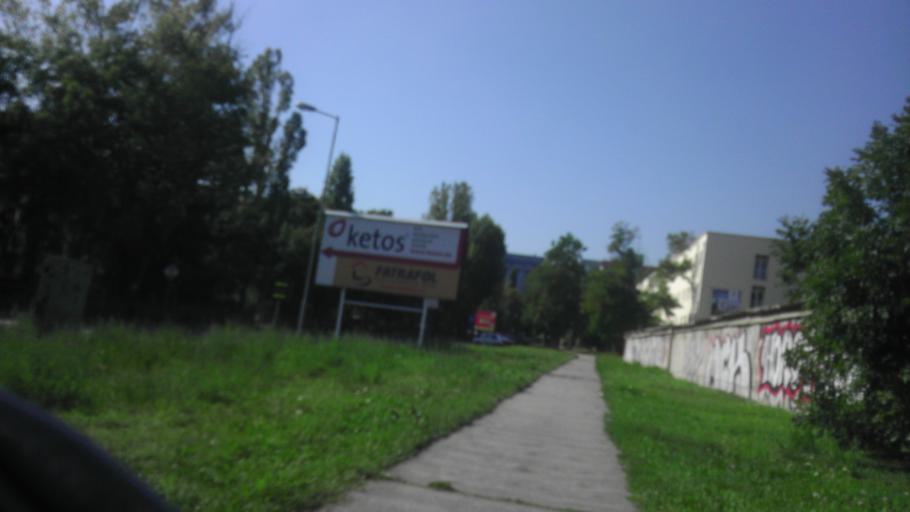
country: SK
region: Bratislavsky
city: Bratislava
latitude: 48.1800
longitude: 17.1378
